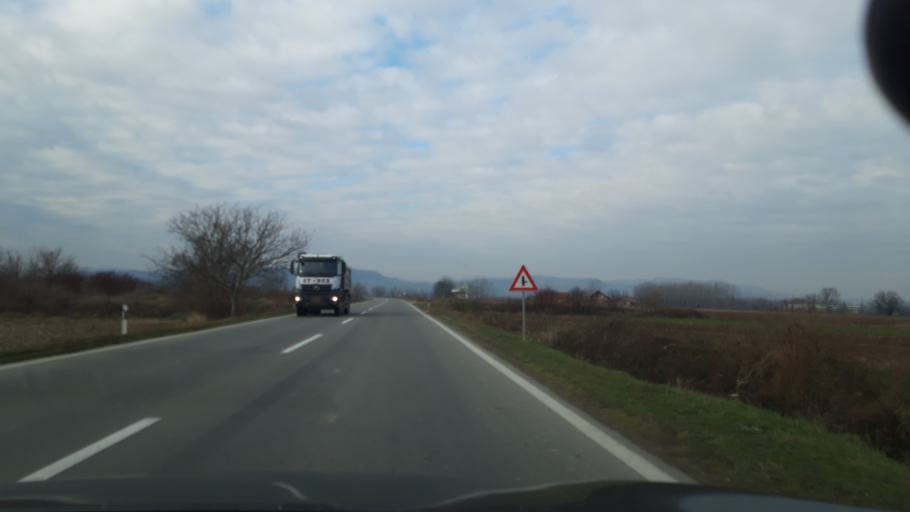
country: RS
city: Lipnicki Sor
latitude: 44.5728
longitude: 19.2243
